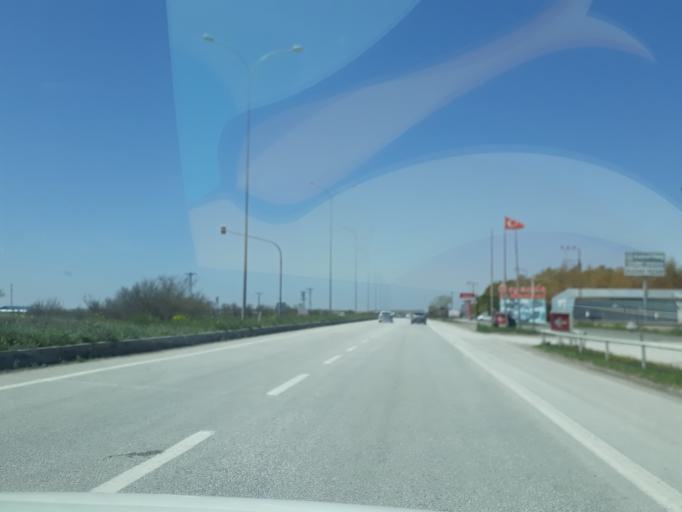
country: TR
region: Konya
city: Karapinar
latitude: 37.7150
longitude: 33.5135
